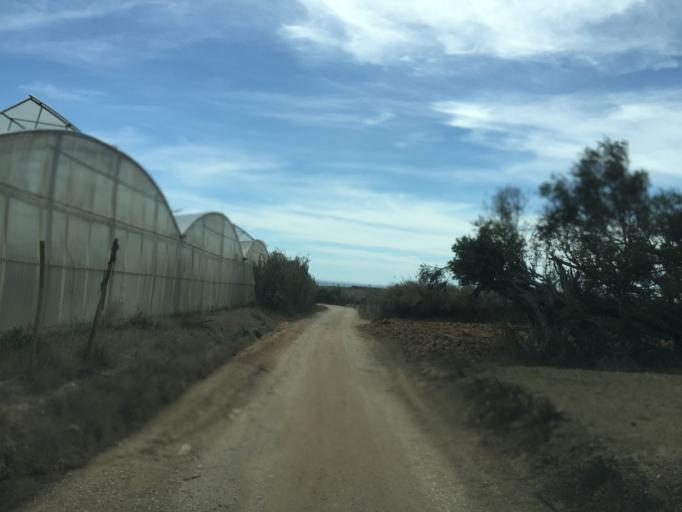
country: PT
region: Lisbon
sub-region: Lourinha
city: Lourinha
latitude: 39.1903
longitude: -9.3459
